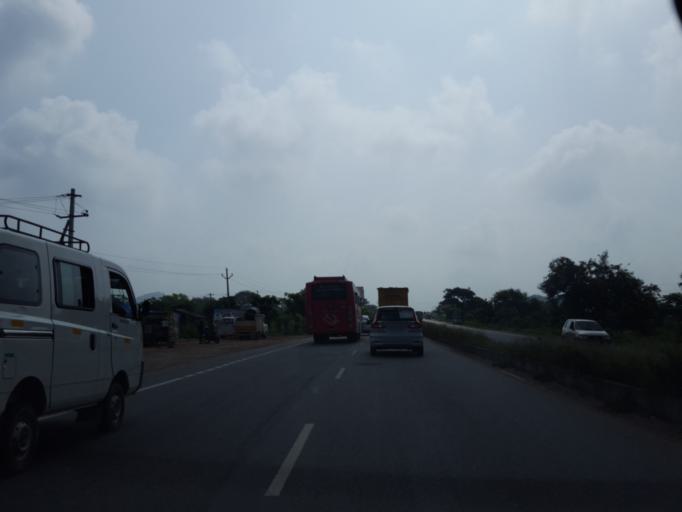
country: IN
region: Telangana
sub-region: Rangareddi
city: Ghatkesar
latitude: 17.2908
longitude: 78.7644
